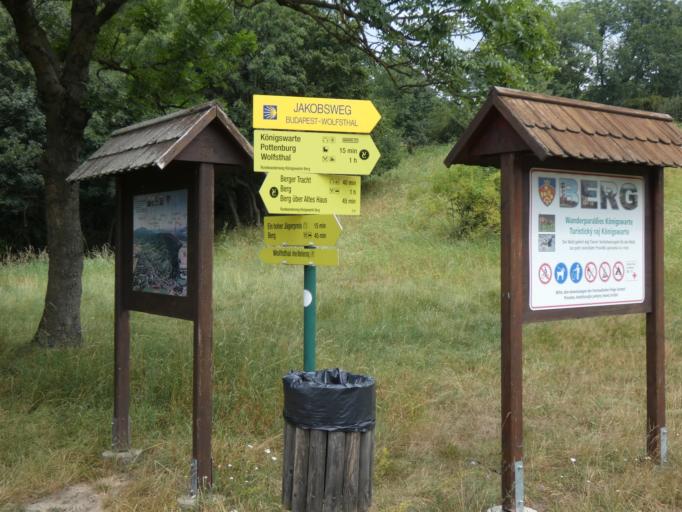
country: AT
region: Lower Austria
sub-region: Politischer Bezirk Bruck an der Leitha
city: Berg
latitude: 48.1149
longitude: 17.0230
